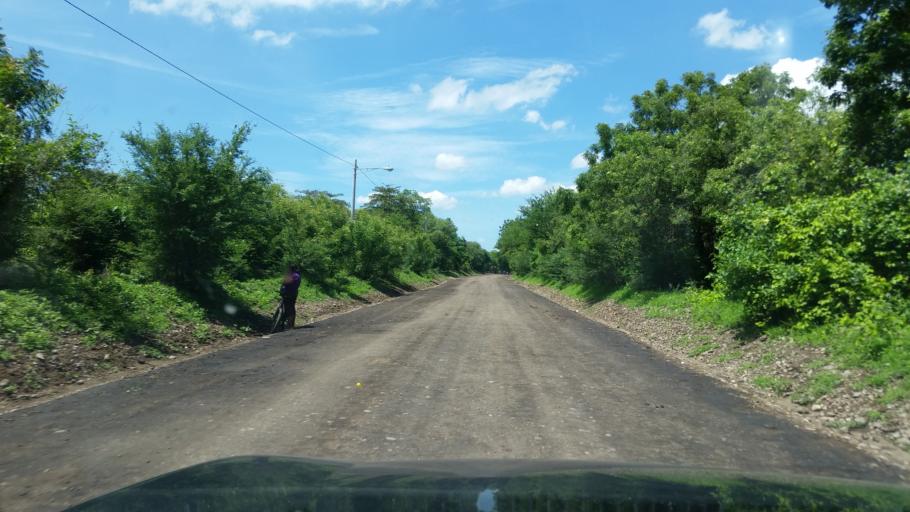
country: NI
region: Chinandega
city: El Viejo
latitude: 12.7488
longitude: -87.1339
